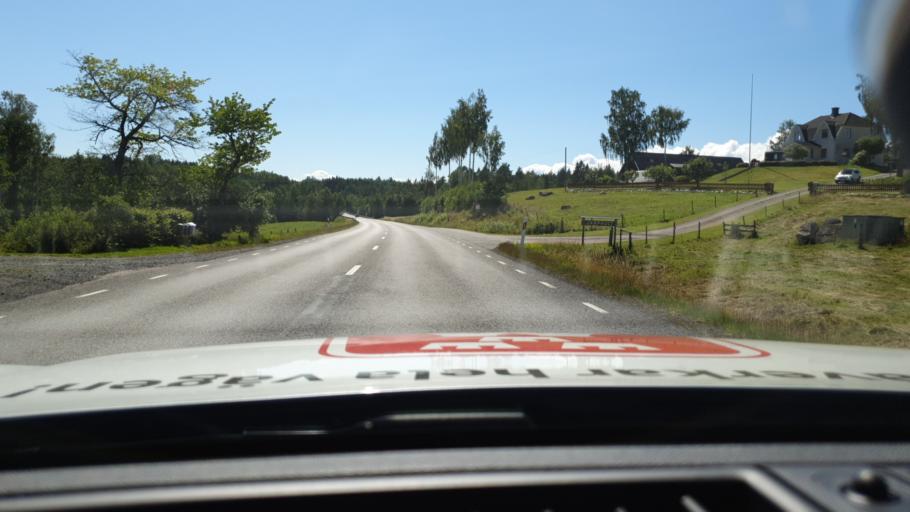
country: SE
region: Joenkoeping
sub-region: Habo Kommun
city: Habo
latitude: 57.9847
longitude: 14.1080
